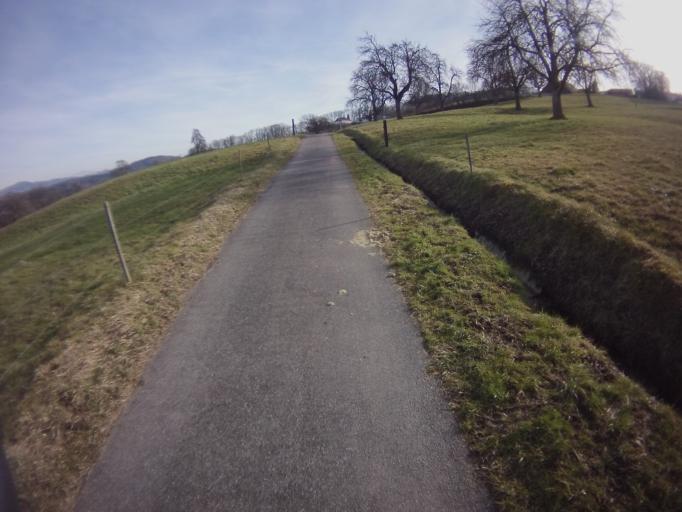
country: CH
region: Zurich
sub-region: Bezirk Dietikon
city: Dietikon / Almend
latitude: 47.3993
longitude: 8.3814
